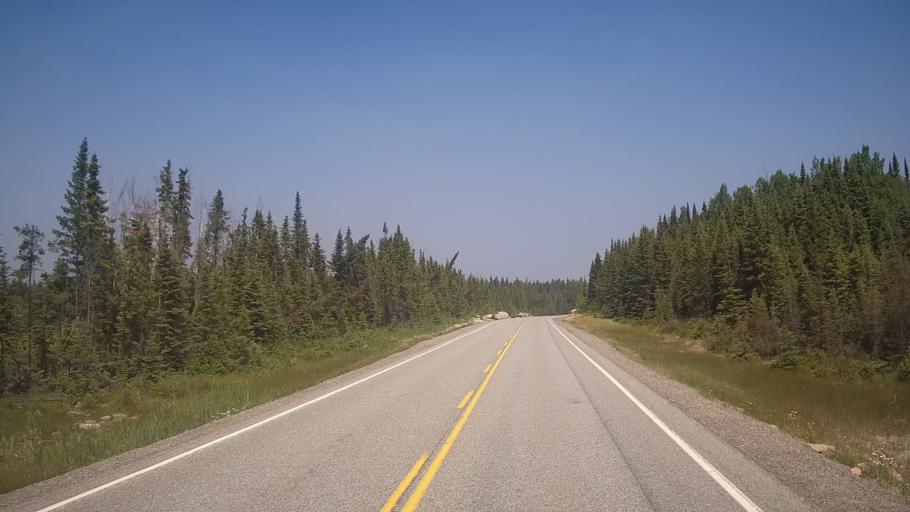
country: CA
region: Ontario
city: Timmins
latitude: 48.0729
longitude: -81.5930
